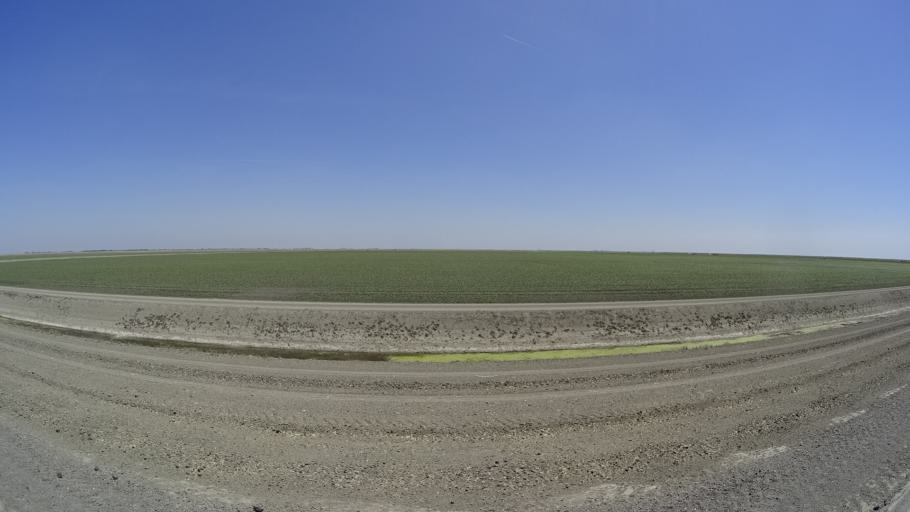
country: US
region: California
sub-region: Kings County
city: Corcoran
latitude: 36.0561
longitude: -119.6437
